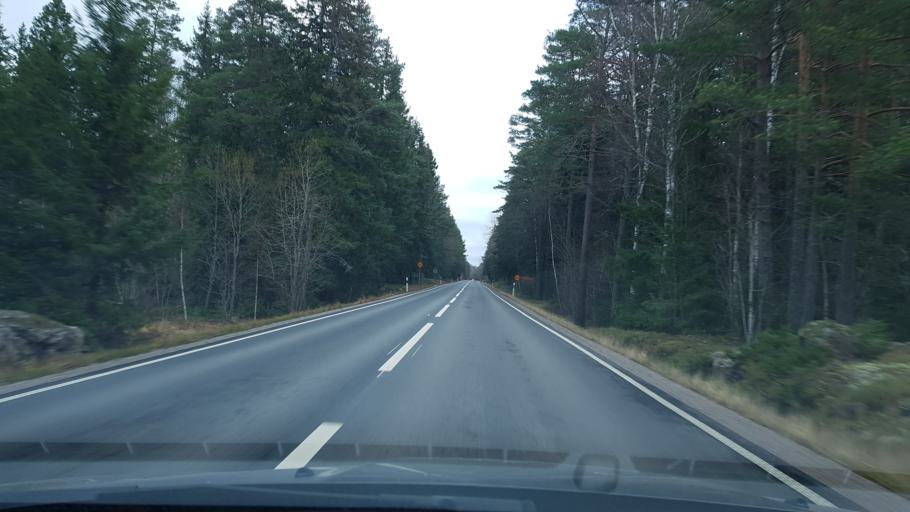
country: SE
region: Stockholm
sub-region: Norrtalje Kommun
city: Skanninge
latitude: 60.0225
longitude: 18.4054
